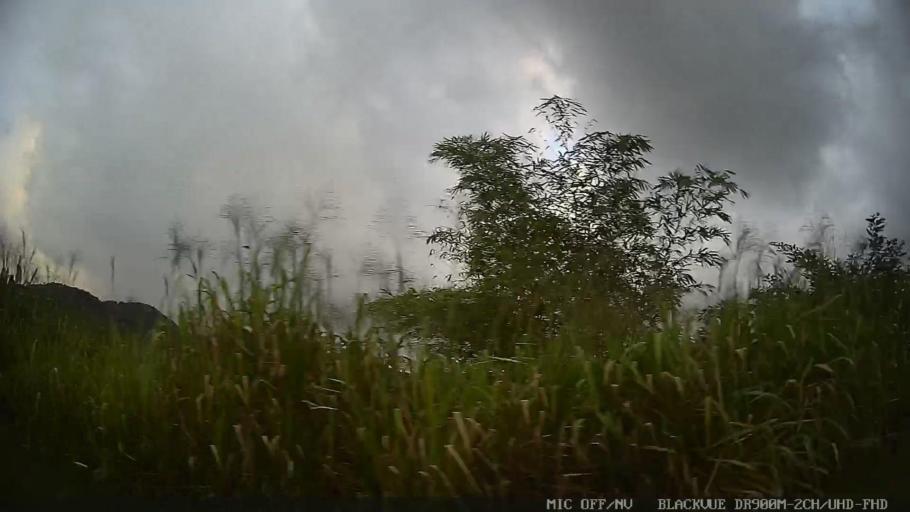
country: BR
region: Sao Paulo
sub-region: Itanhaem
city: Itanhaem
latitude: -24.0961
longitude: -46.8001
